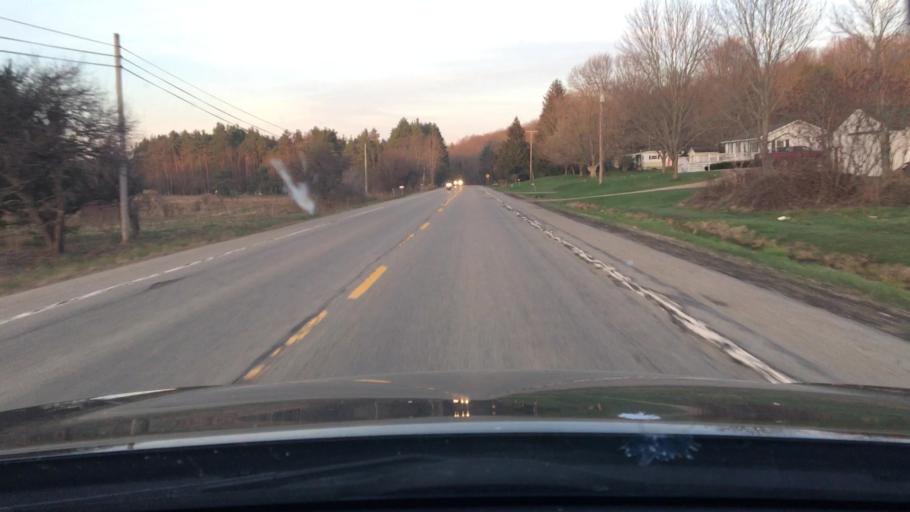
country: US
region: New York
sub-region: Cattaraugus County
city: Randolph
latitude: 42.1771
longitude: -78.9294
